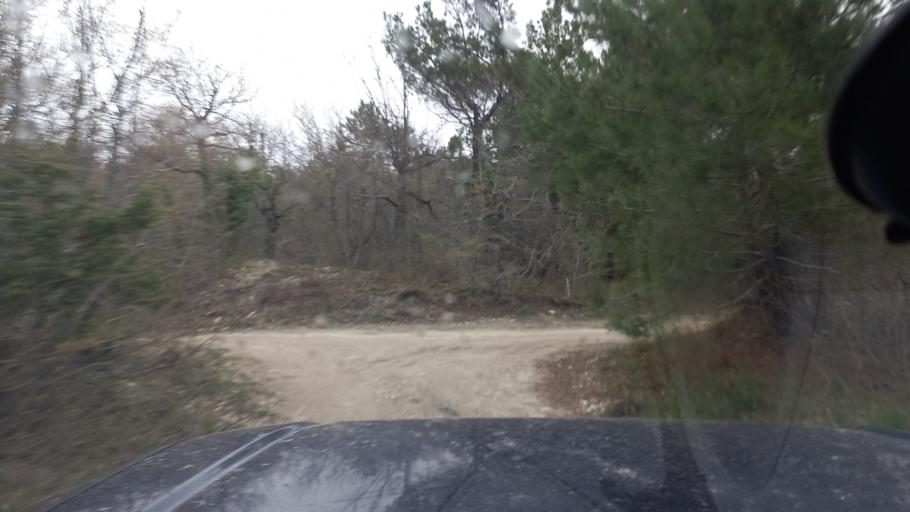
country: RU
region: Krasnodarskiy
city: Dzhubga
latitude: 44.3197
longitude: 38.6788
